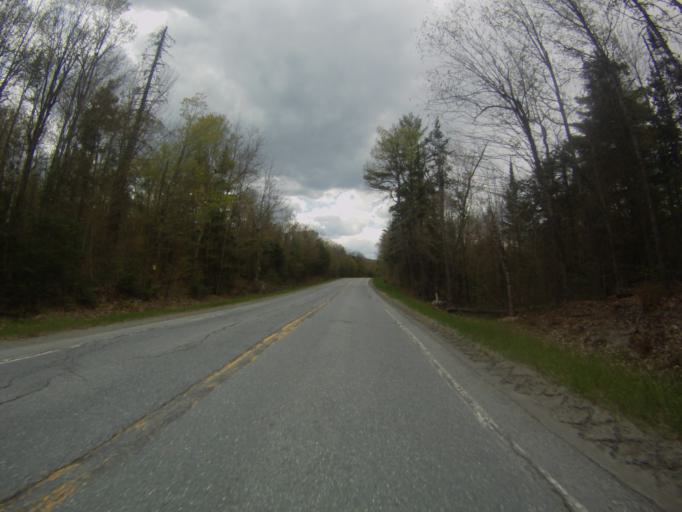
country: US
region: New York
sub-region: Essex County
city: Mineville
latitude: 44.0973
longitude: -73.5592
